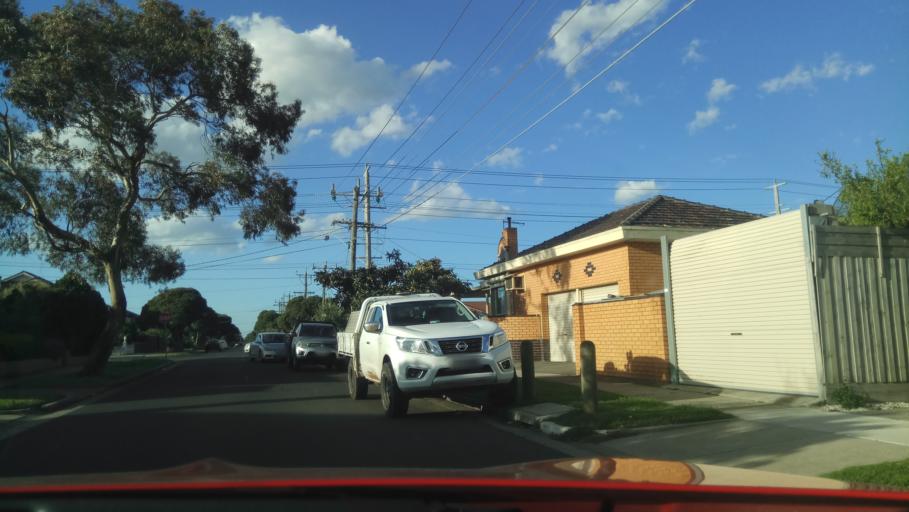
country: AU
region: Victoria
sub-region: Hobsons Bay
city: Altona North
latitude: -37.8307
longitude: 144.8385
